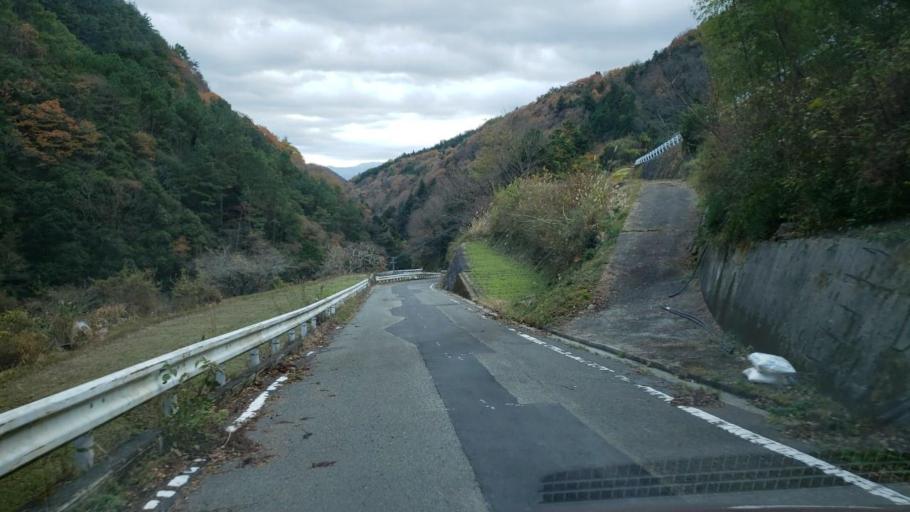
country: JP
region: Tokushima
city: Wakimachi
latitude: 34.1503
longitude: 134.2280
